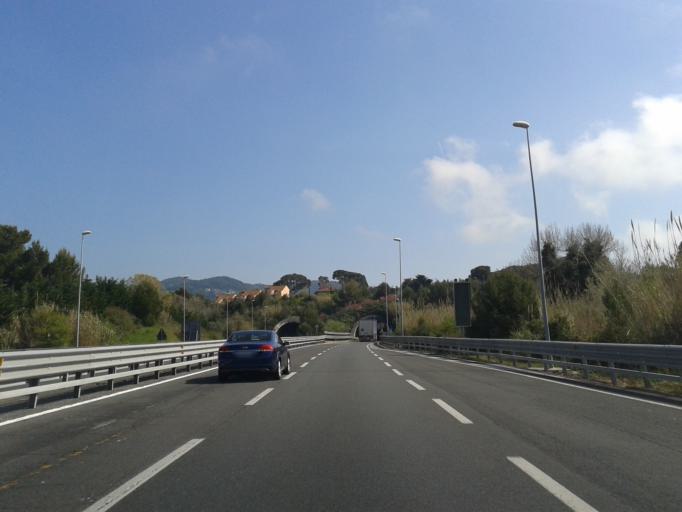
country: IT
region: Tuscany
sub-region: Provincia di Livorno
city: Livorno
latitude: 43.5109
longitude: 10.3344
